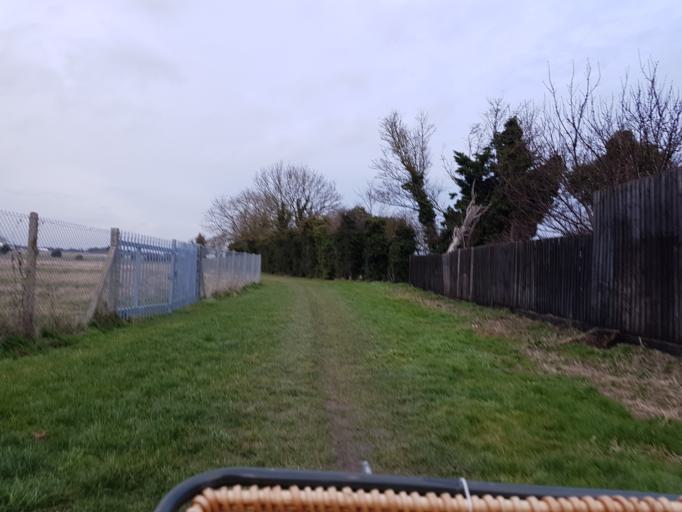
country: GB
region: England
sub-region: Cambridgeshire
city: Fulbourn
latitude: 52.1964
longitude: 0.1784
